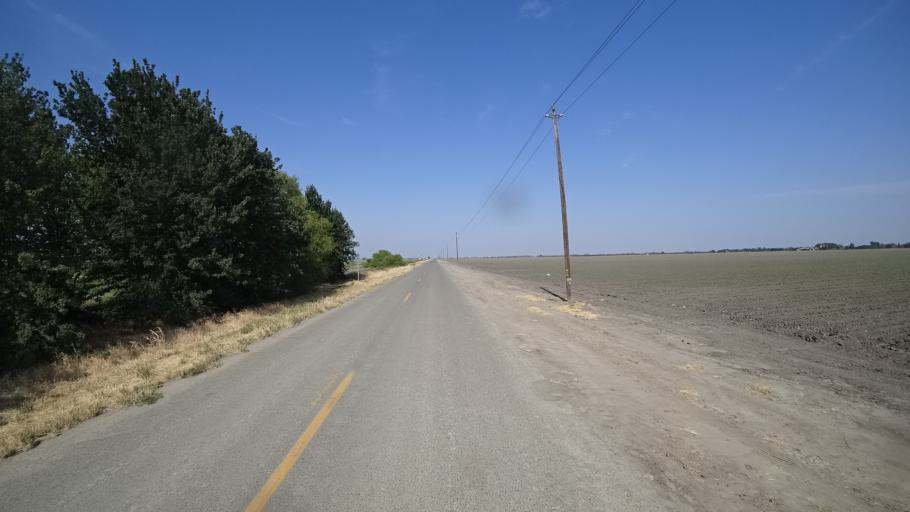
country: US
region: California
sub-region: Kings County
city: Lemoore
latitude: 36.3135
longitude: -119.8354
